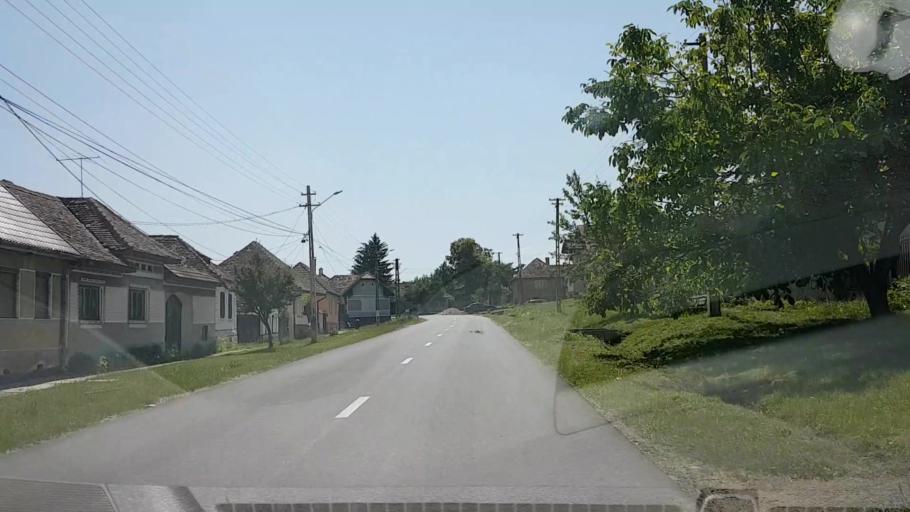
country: RO
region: Sibiu
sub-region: Comuna Merghindeal
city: Merghindeal
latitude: 45.9641
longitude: 24.7332
